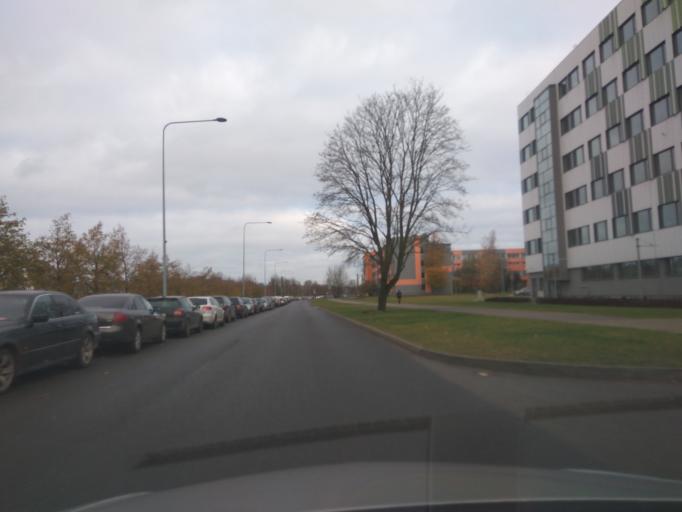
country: LV
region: Riga
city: Riga
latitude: 56.9511
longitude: 24.0788
